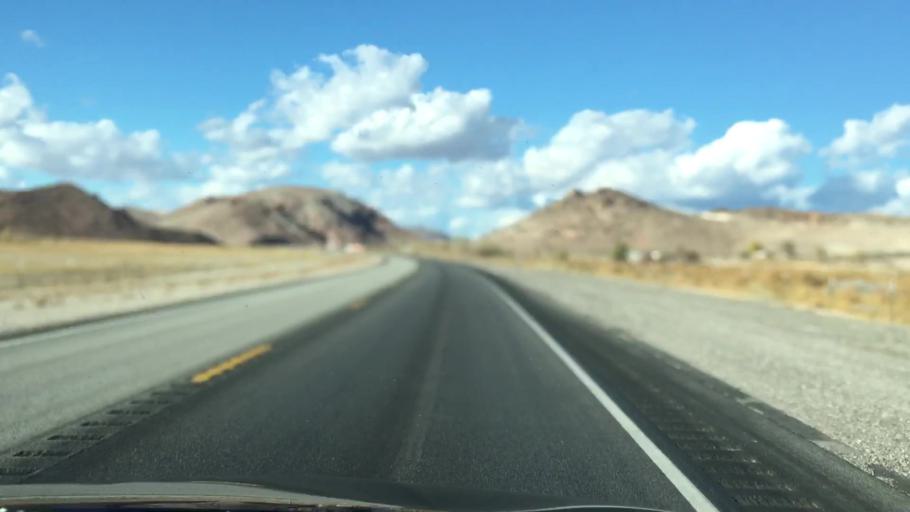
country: US
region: Nevada
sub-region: Nye County
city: Beatty
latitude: 36.9667
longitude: -116.7188
